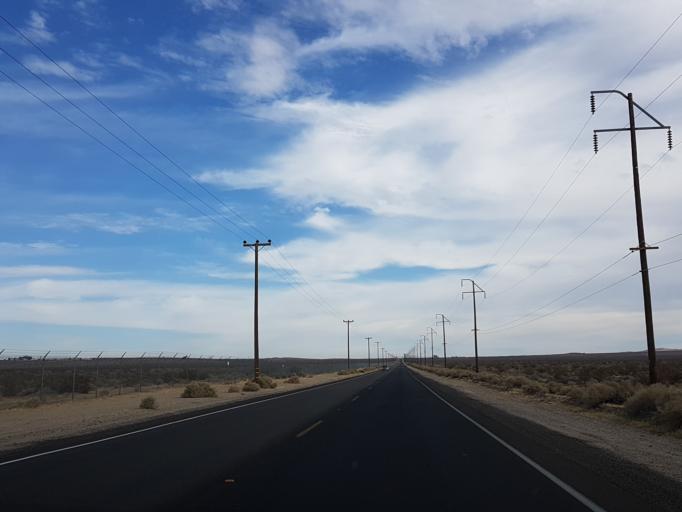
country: US
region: California
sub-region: Kern County
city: Ridgecrest
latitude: 35.6225
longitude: -117.6318
